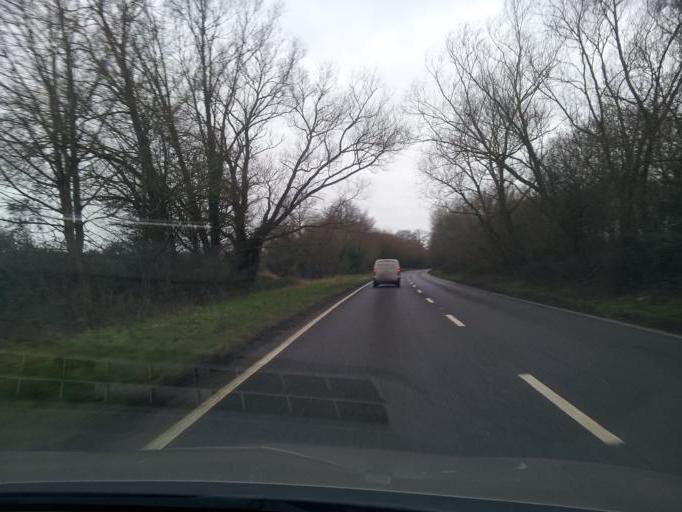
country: GB
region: England
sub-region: Suffolk
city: Botesdale
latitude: 52.3485
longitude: 1.0493
